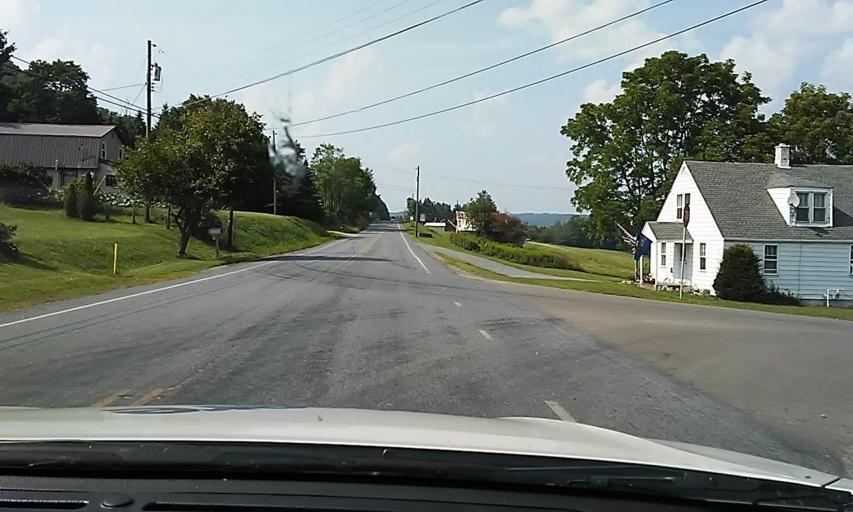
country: US
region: New York
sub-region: Allegany County
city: Wellsville
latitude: 41.9733
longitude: -77.8609
